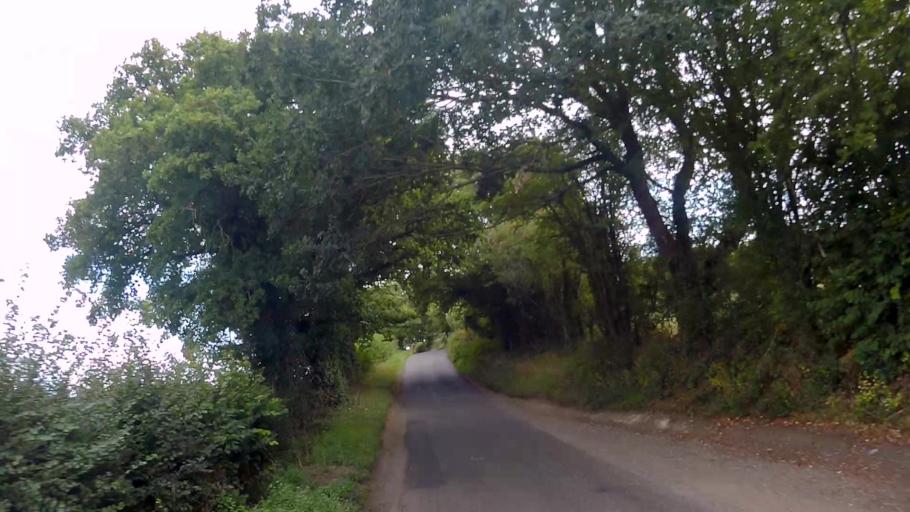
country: GB
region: England
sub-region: Hampshire
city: Kings Worthy
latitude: 51.1495
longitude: -1.2213
